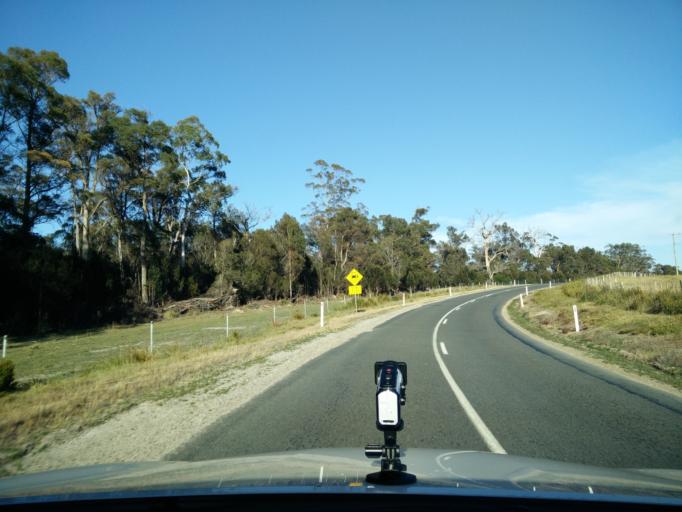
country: AU
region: Tasmania
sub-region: Break O'Day
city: St Helens
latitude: -41.2827
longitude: 148.1301
